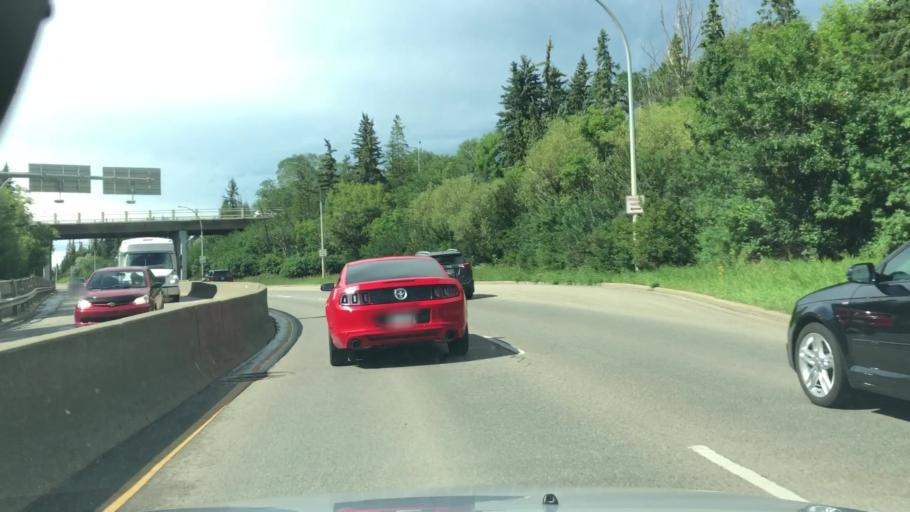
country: CA
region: Alberta
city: Edmonton
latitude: 53.5469
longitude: -113.5448
